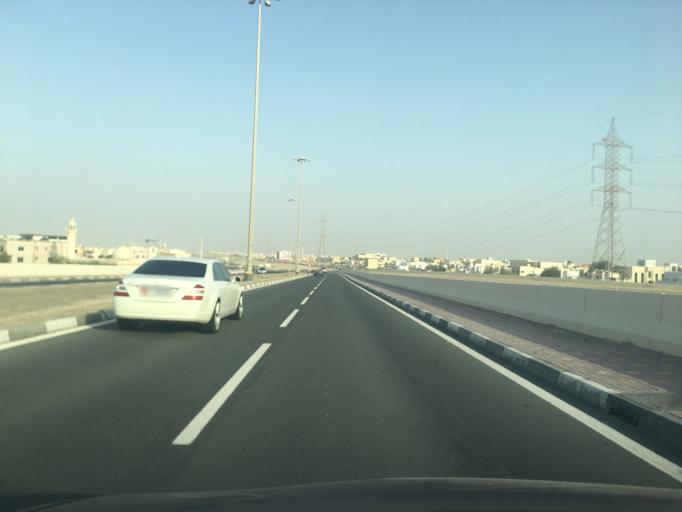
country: AE
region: Abu Dhabi
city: Abu Dhabi
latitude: 24.3264
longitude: 54.6233
